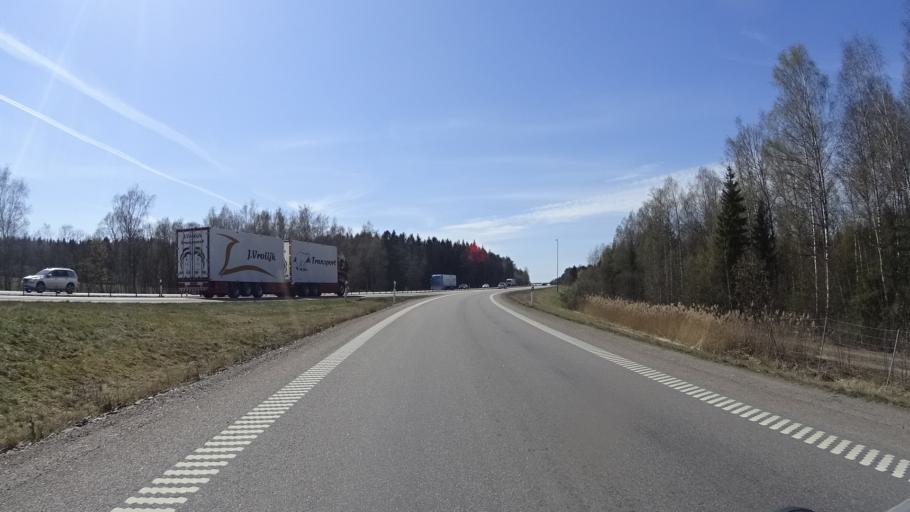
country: SE
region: OEstergoetland
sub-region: Mjolby Kommun
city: Mantorp
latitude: 58.3532
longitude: 15.2070
